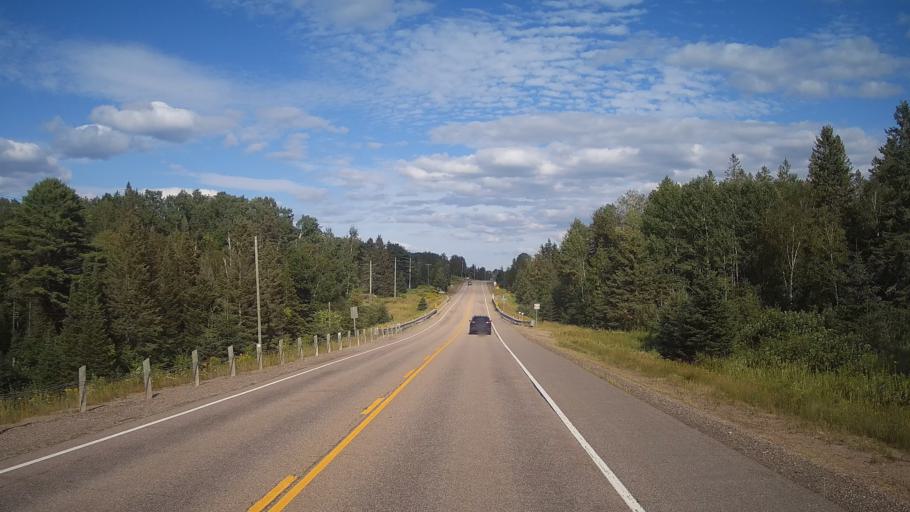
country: CA
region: Ontario
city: Mattawa
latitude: 46.2699
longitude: -79.0509
